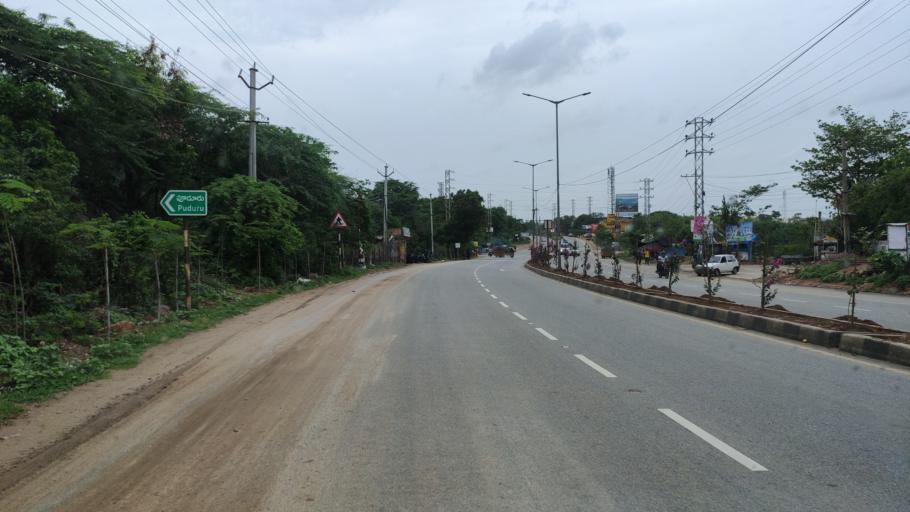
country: IN
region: Telangana
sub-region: Rangareddi
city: Secunderabad
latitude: 17.5948
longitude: 78.5692
